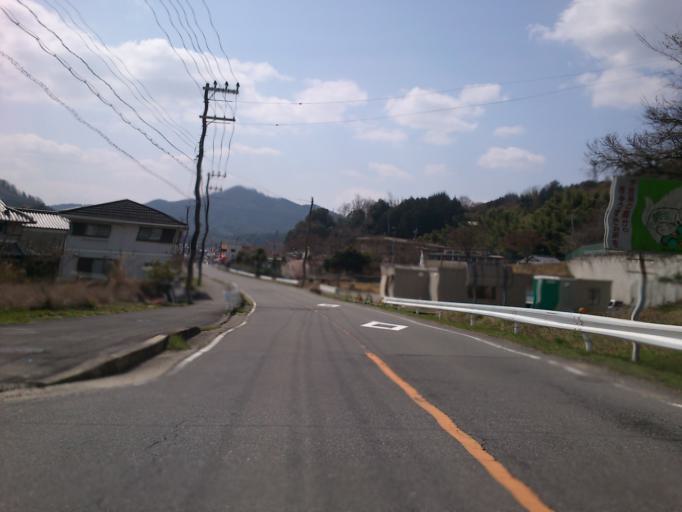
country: JP
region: Kyoto
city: Uji
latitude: 34.8040
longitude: 135.9099
